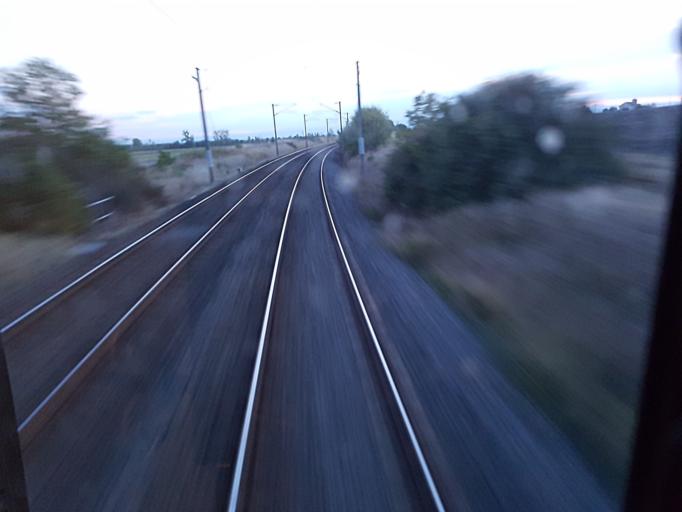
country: FR
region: Auvergne
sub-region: Departement du Puy-de-Dome
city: Randan
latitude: 45.9881
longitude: 3.3203
